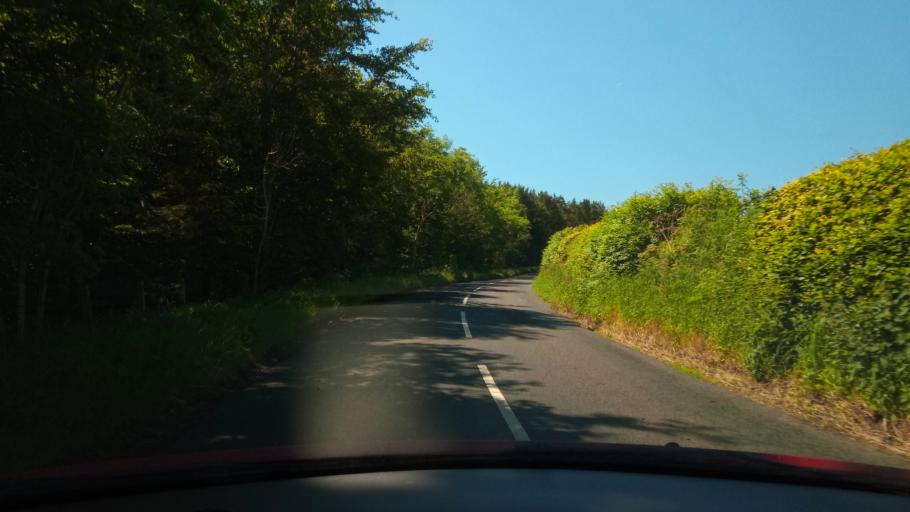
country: GB
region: Scotland
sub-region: The Scottish Borders
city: Duns
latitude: 55.7771
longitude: -2.3999
